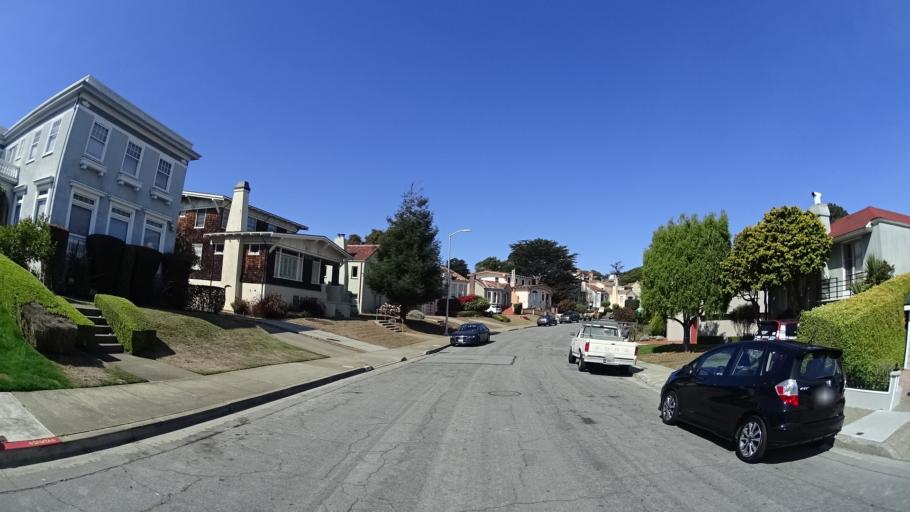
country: US
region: California
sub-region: San Mateo County
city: Daly City
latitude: 37.7248
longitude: -122.4700
